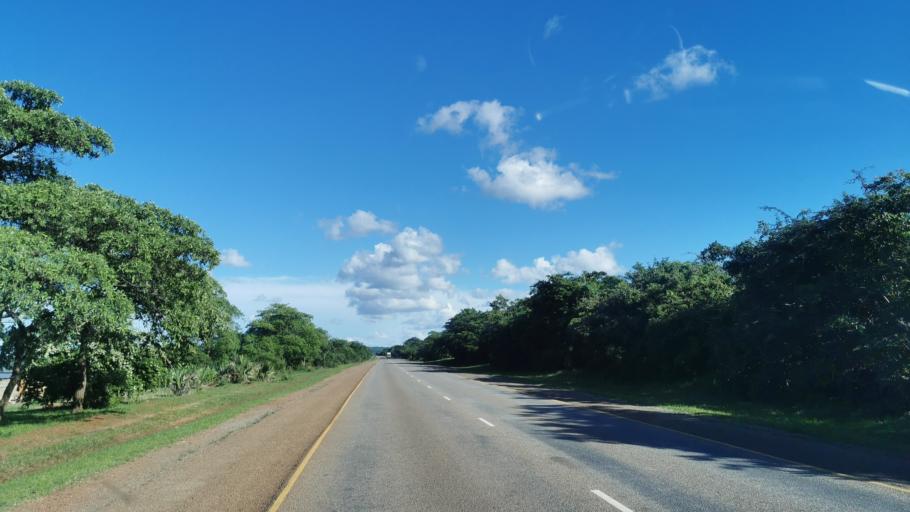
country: TZ
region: Geita
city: Masumbwe
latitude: -3.7200
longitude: 32.2965
